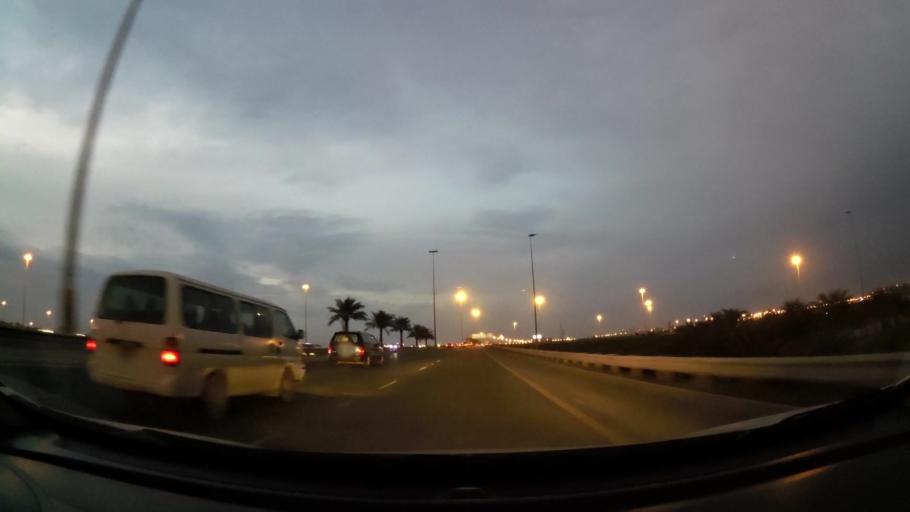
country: BH
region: Northern
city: Madinat `Isa
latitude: 26.1834
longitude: 50.5031
